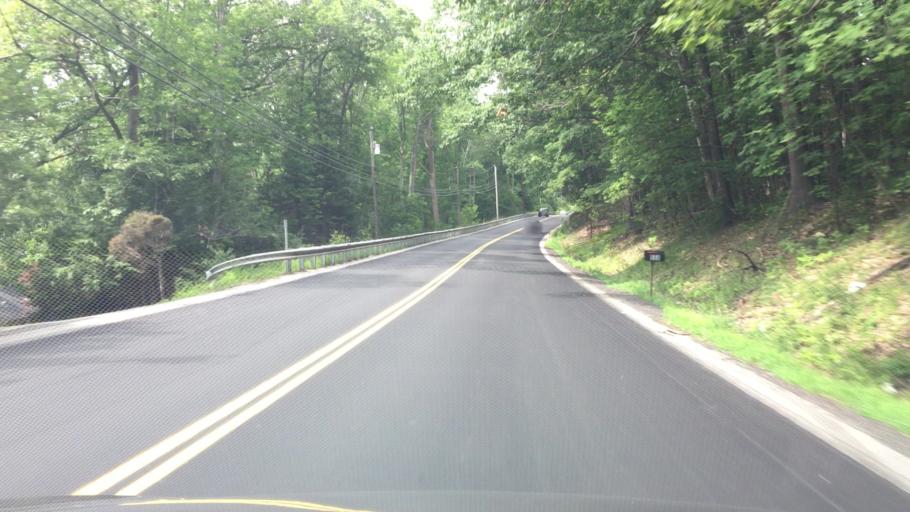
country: US
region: Maine
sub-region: Waldo County
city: Winterport
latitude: 44.6121
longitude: -68.8237
